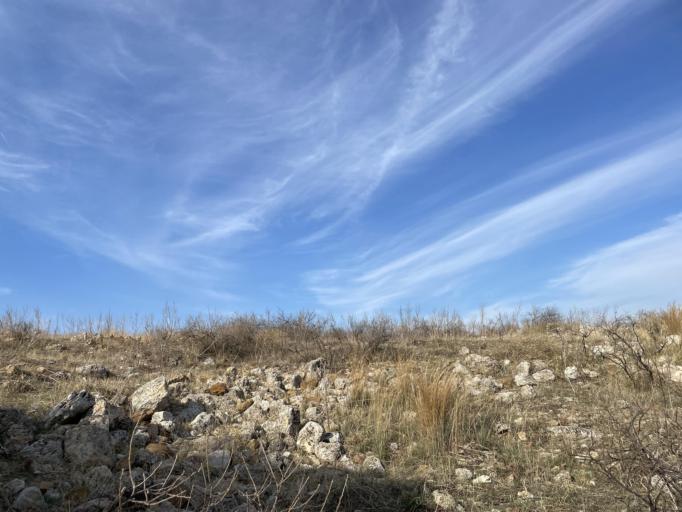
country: TR
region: Antalya
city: Aksu
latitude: 36.9677
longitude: 30.8560
